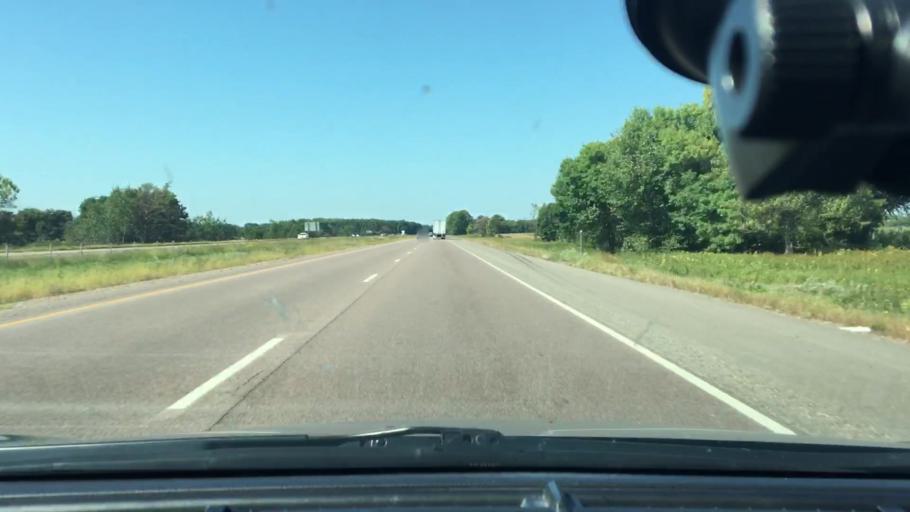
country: US
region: Wisconsin
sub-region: Eau Claire County
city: Eau Claire
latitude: 44.8497
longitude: -91.6311
